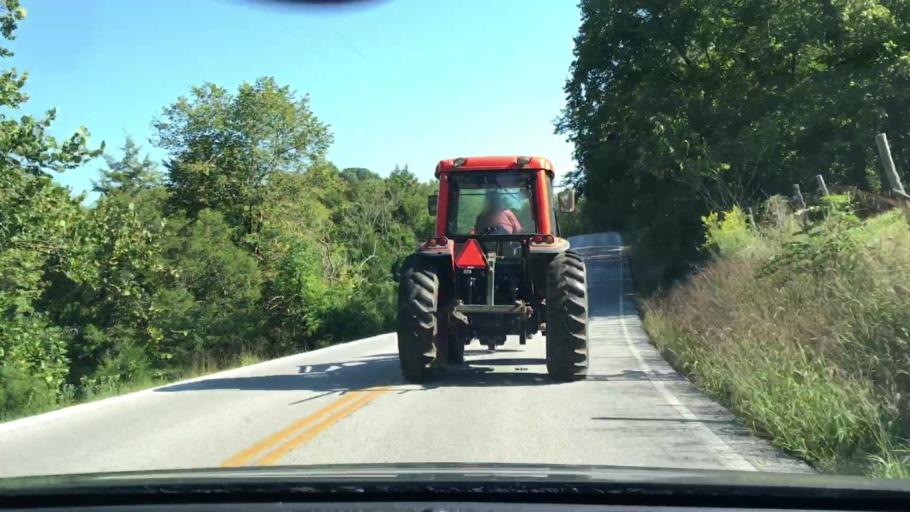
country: US
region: Tennessee
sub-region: Smith County
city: Carthage
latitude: 36.3004
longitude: -85.9533
